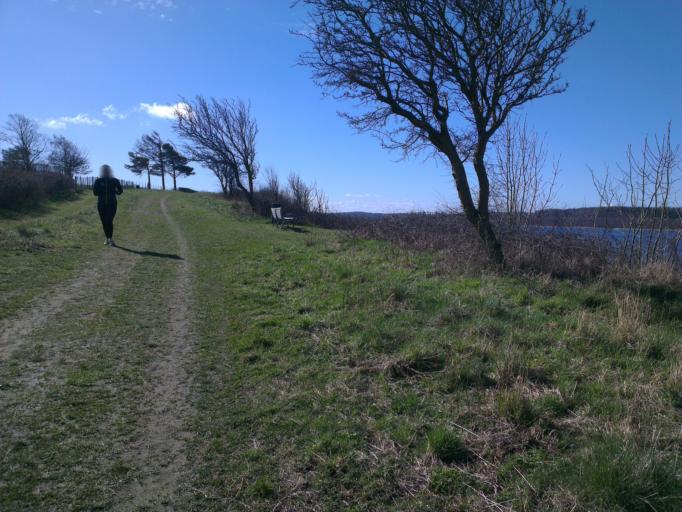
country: DK
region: Capital Region
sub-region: Frederikssund Kommune
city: Frederikssund
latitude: 55.8549
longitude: 12.0456
